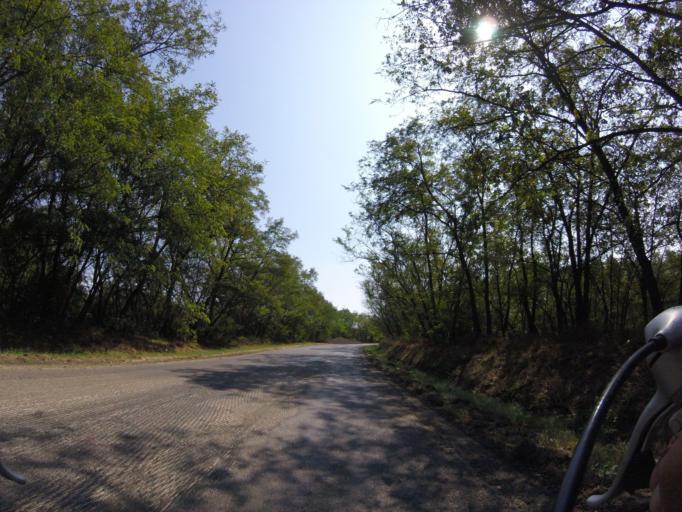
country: HU
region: Szabolcs-Szatmar-Bereg
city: Anarcs
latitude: 48.1675
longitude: 22.1175
